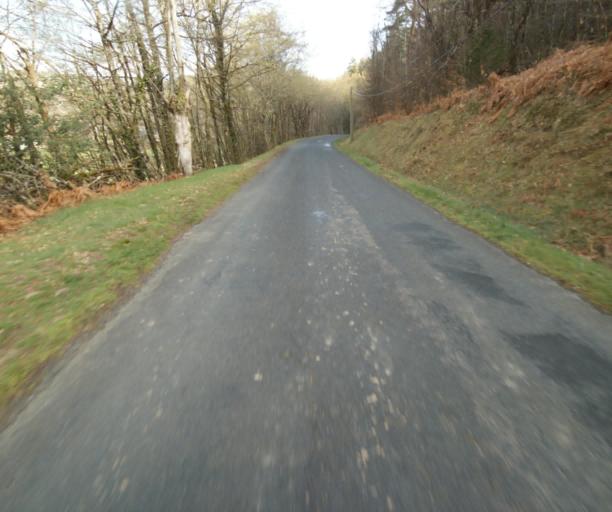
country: FR
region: Limousin
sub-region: Departement de la Correze
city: Correze
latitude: 45.3391
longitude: 1.8234
